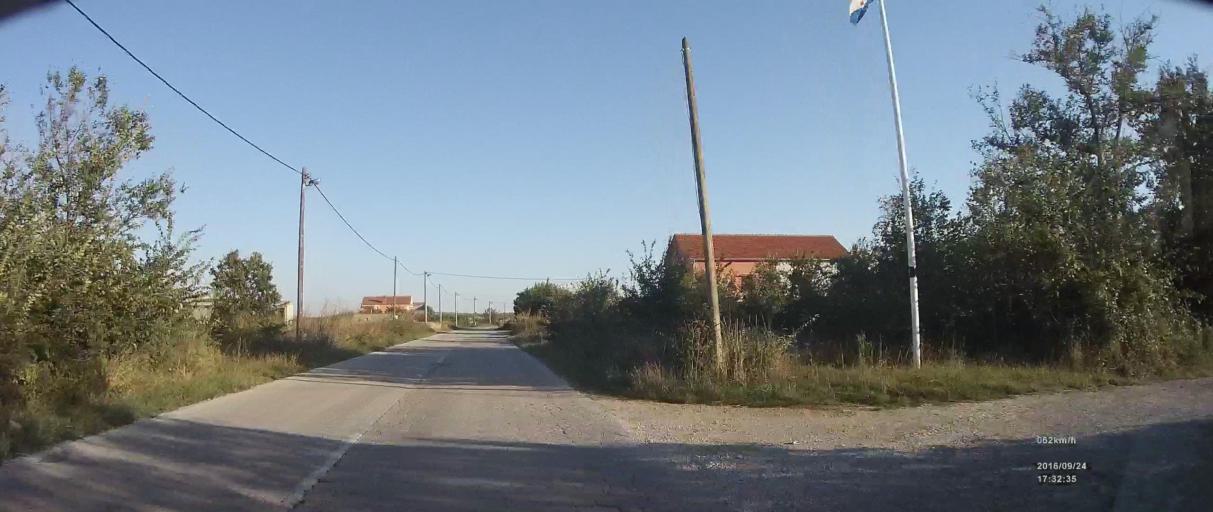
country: HR
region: Zadarska
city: Posedarje
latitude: 44.1811
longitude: 15.4514
